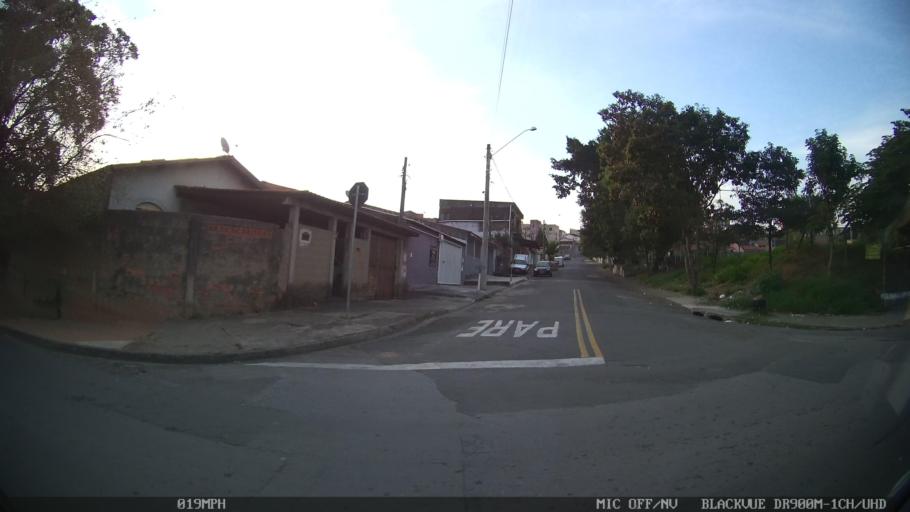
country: BR
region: Sao Paulo
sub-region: Campinas
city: Campinas
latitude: -22.9832
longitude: -47.1317
